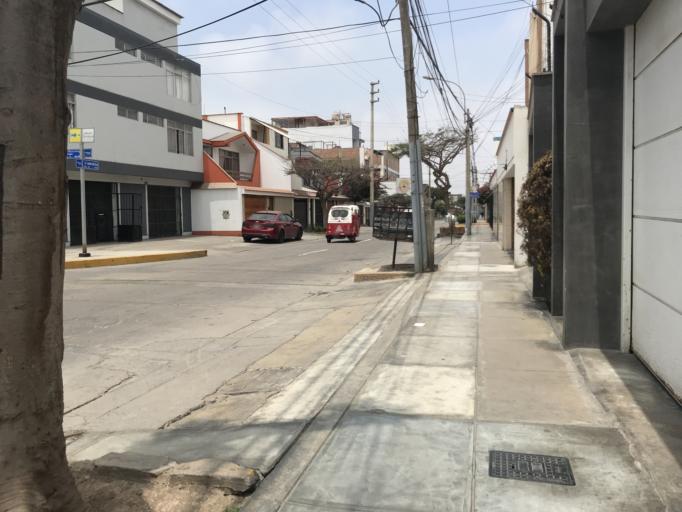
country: PE
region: Lima
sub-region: Lima
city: San Isidro
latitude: -12.0816
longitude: -77.0767
